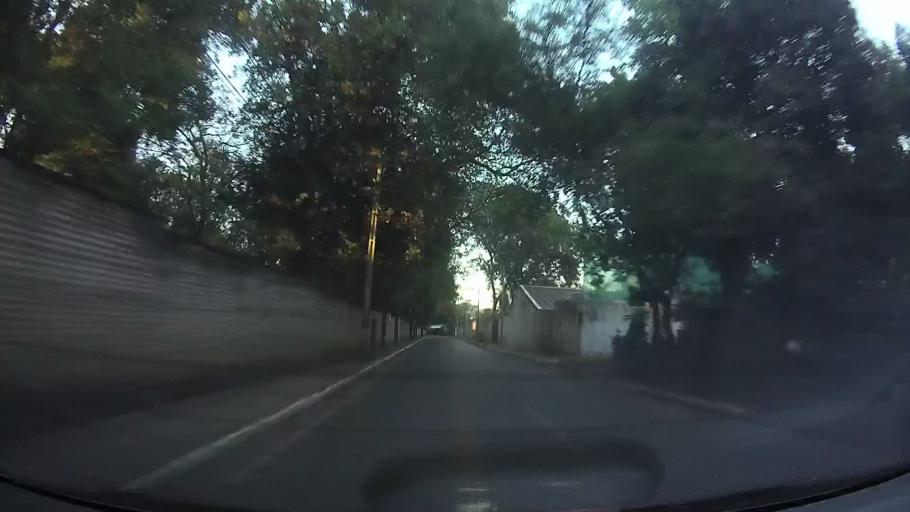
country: PY
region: Central
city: Fernando de la Mora
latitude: -25.3321
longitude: -57.5460
